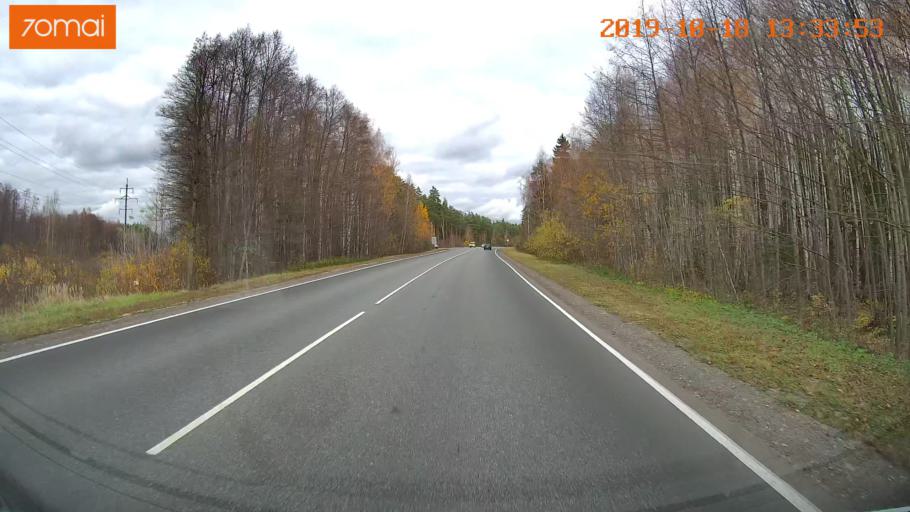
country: RU
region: Rjazan
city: Solotcha
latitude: 54.8488
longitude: 39.9435
